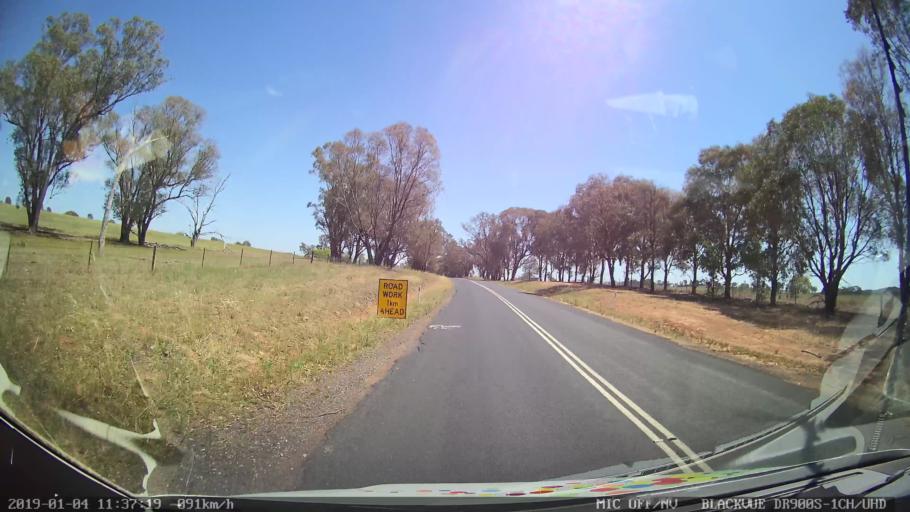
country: AU
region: New South Wales
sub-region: Cabonne
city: Molong
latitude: -33.0337
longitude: 148.8081
